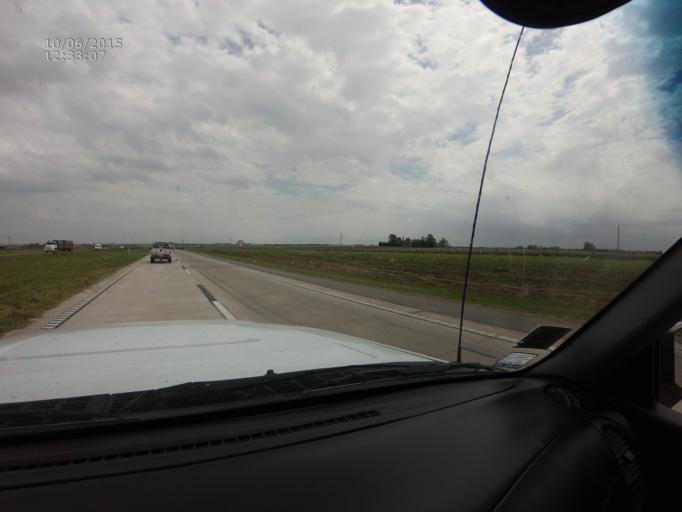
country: AR
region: Santa Fe
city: Carcarana
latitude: -32.8780
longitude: -61.1606
